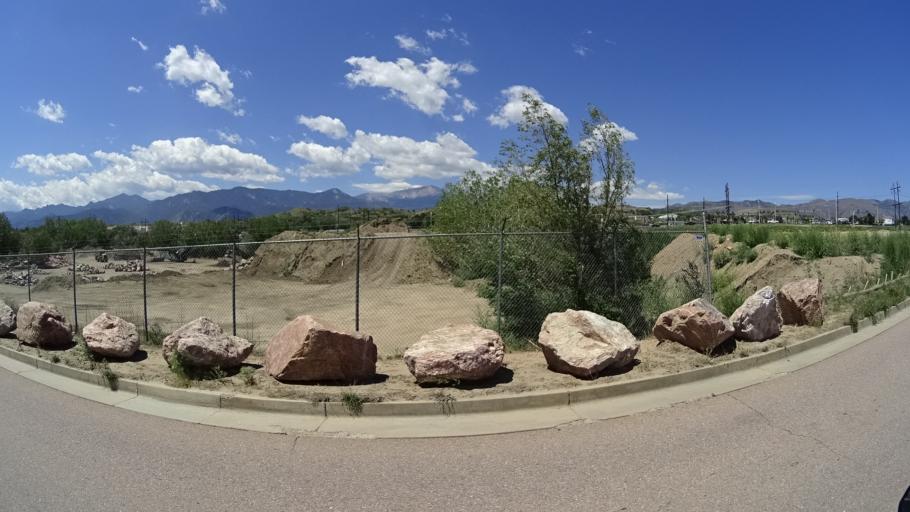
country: US
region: Colorado
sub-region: El Paso County
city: Colorado Springs
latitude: 38.8749
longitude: -104.8316
